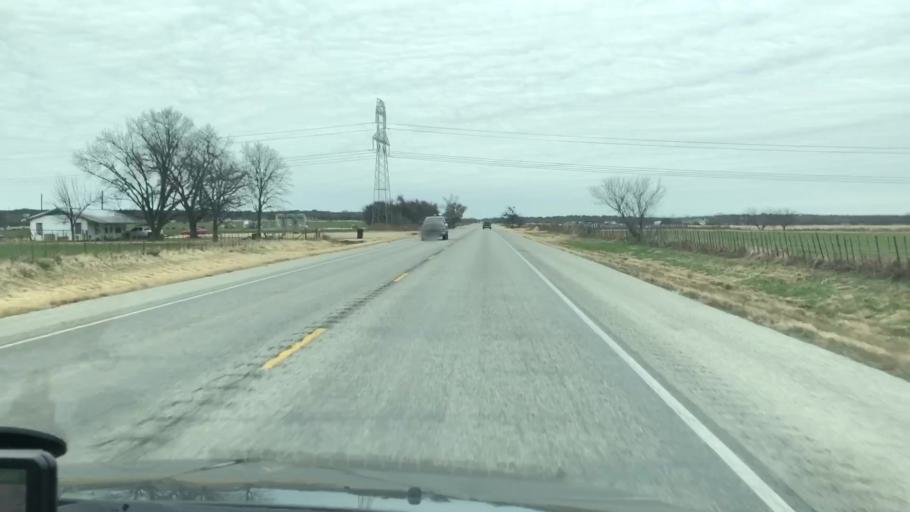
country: US
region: Texas
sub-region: Palo Pinto County
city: Mineral Wells
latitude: 32.9292
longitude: -98.0713
